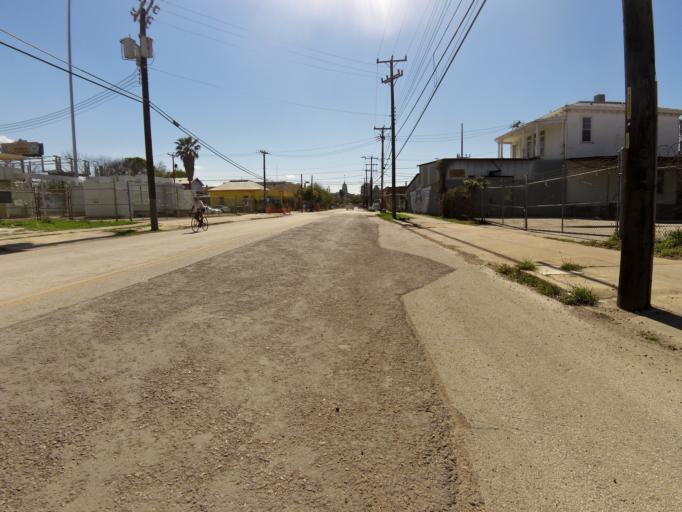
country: US
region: Texas
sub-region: Bexar County
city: San Antonio
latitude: 29.4332
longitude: -98.4804
